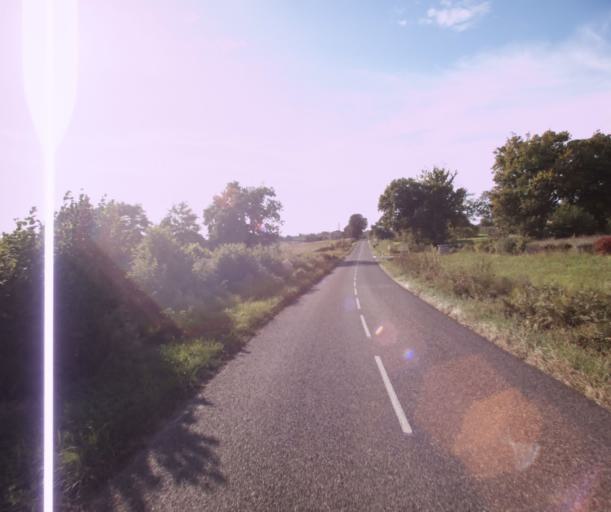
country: FR
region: Midi-Pyrenees
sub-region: Departement du Gers
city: Eauze
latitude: 43.8578
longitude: 0.0484
